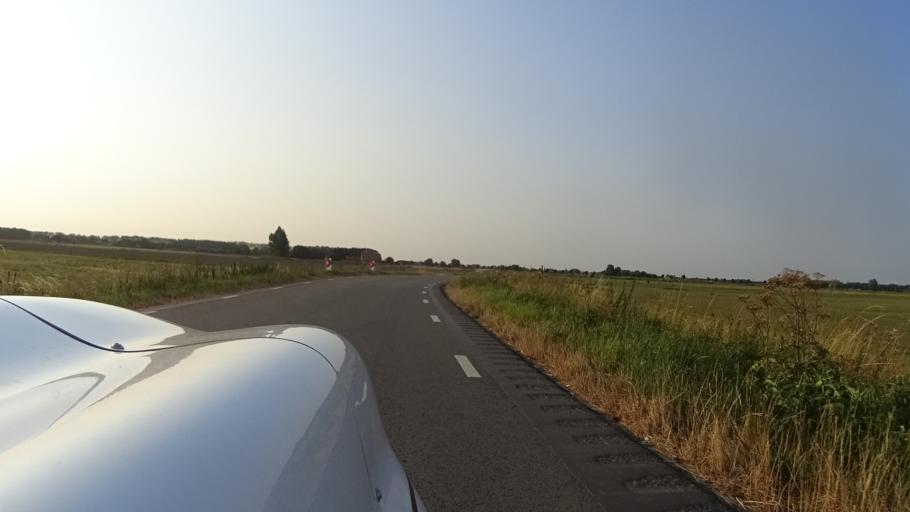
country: NL
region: North Brabant
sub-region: Gemeente Oss
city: Oss
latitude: 51.8504
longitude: 5.5224
